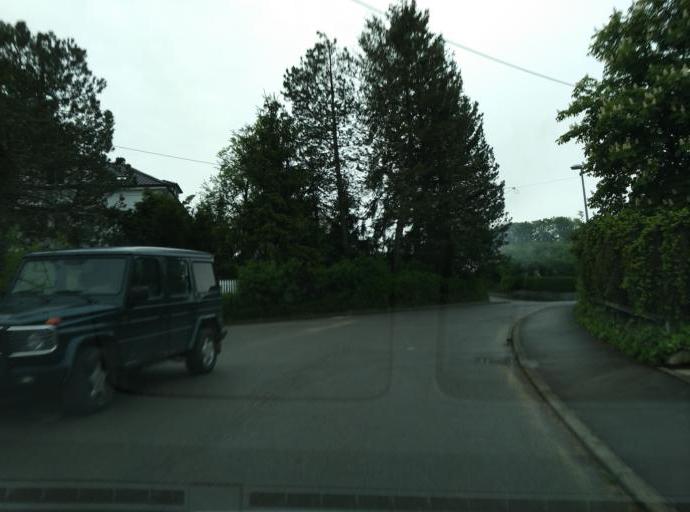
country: DE
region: Baden-Wuerttemberg
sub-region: Tuebingen Region
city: Wannweil
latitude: 48.5139
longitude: 9.1474
